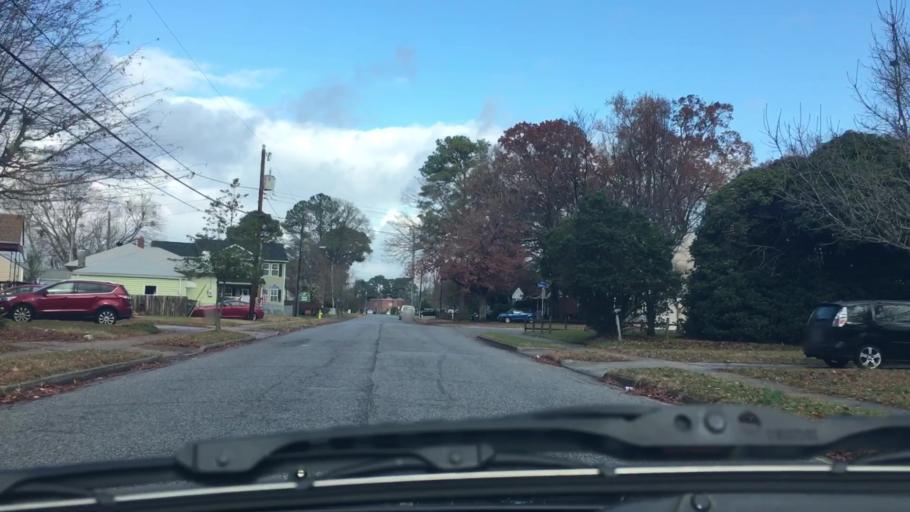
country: US
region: Virginia
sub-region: City of Norfolk
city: Norfolk
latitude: 36.9253
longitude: -76.2458
